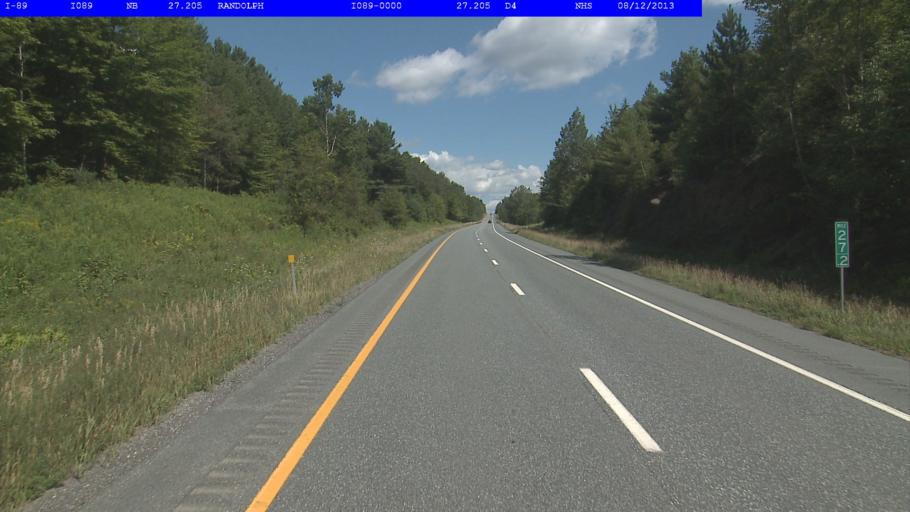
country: US
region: Vermont
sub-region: Orange County
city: Randolph
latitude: 43.8922
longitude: -72.6164
